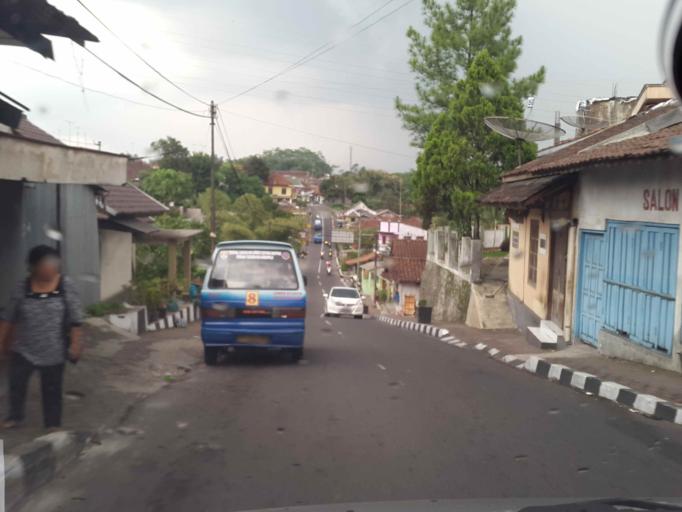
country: ID
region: Central Java
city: Magelang
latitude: -7.4833
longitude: 110.2338
